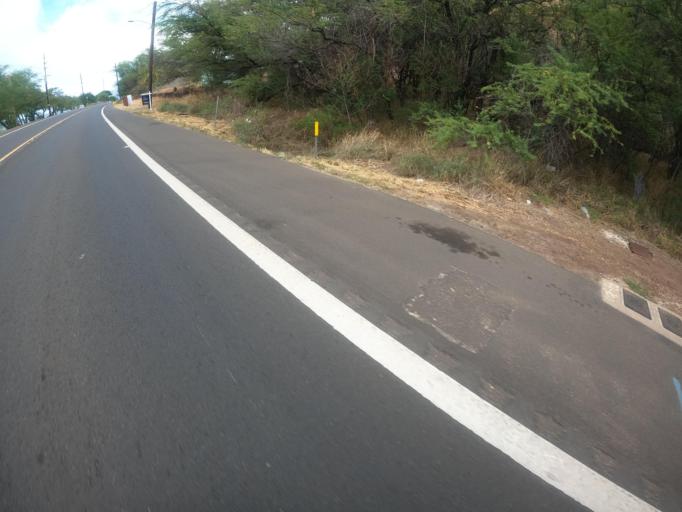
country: US
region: Hawaii
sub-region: Honolulu County
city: Makaha
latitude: 21.4839
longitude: -158.2281
